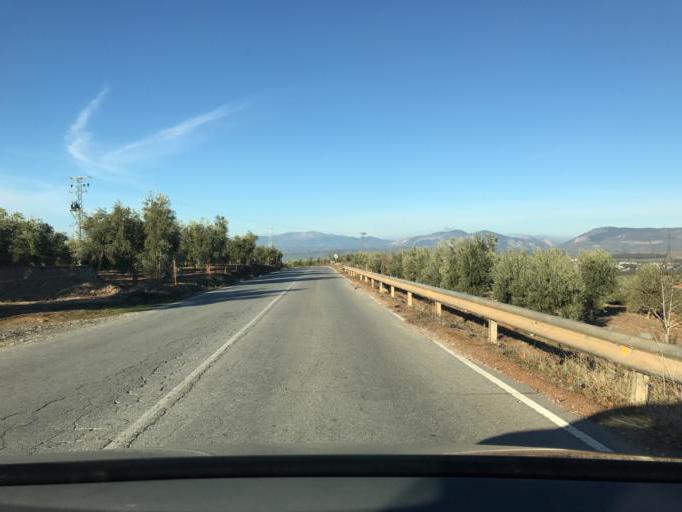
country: ES
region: Andalusia
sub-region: Provincia de Granada
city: Calicasas
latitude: 37.2661
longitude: -3.6396
